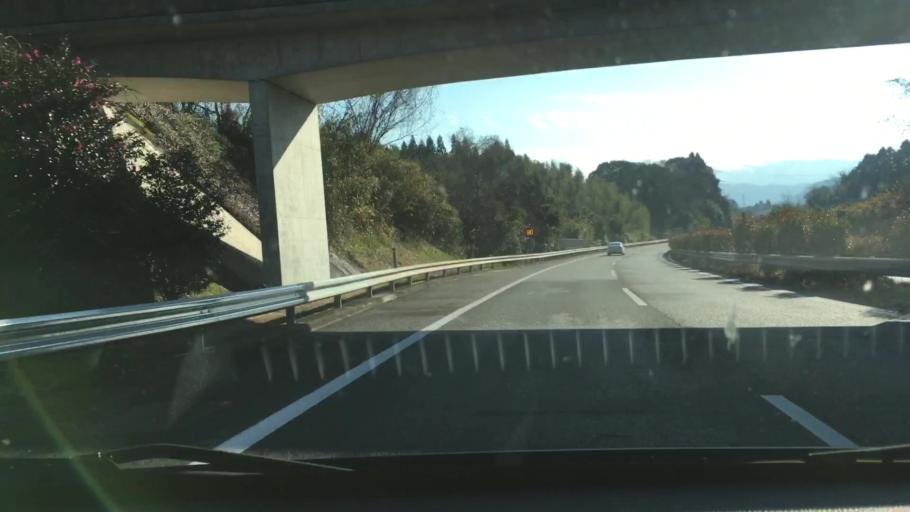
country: JP
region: Kumamoto
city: Hitoyoshi
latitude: 32.2186
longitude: 130.7802
